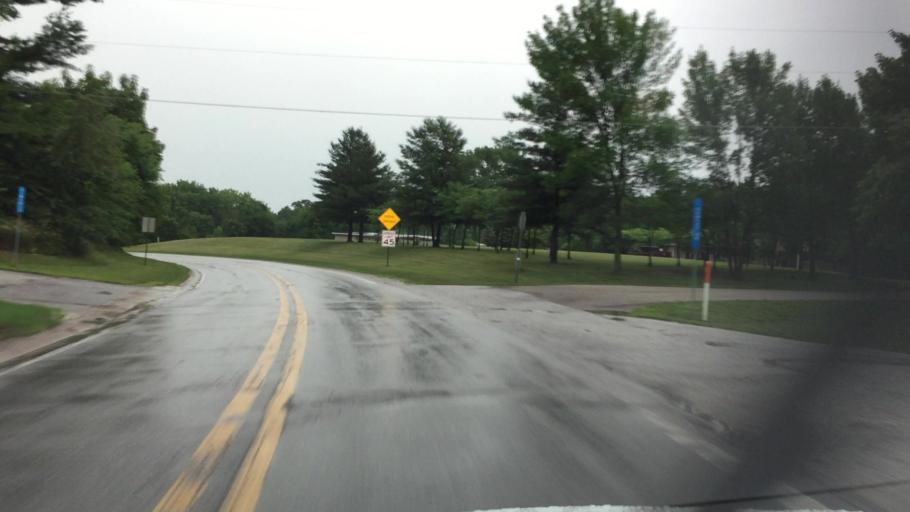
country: US
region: Illinois
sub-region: Hancock County
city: Carthage
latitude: 40.4233
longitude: -91.1364
